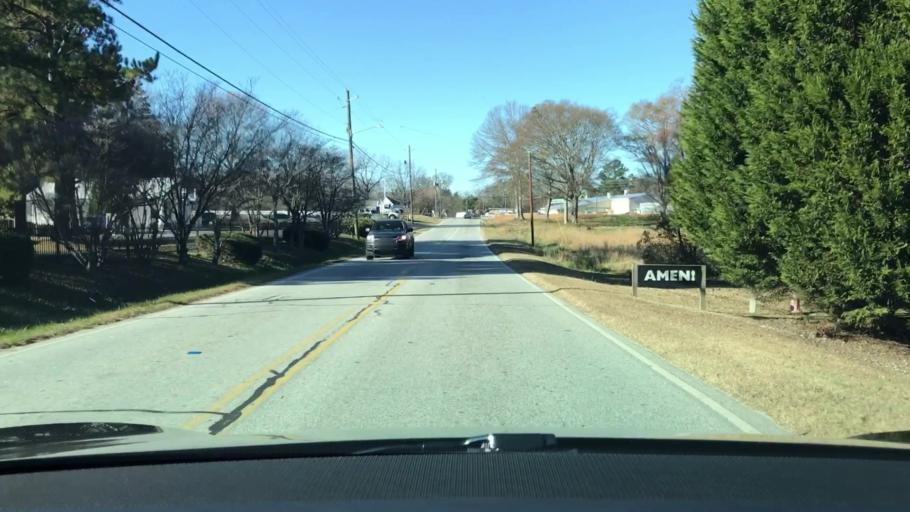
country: US
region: Georgia
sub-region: Barrow County
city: Auburn
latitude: 34.0032
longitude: -83.8101
